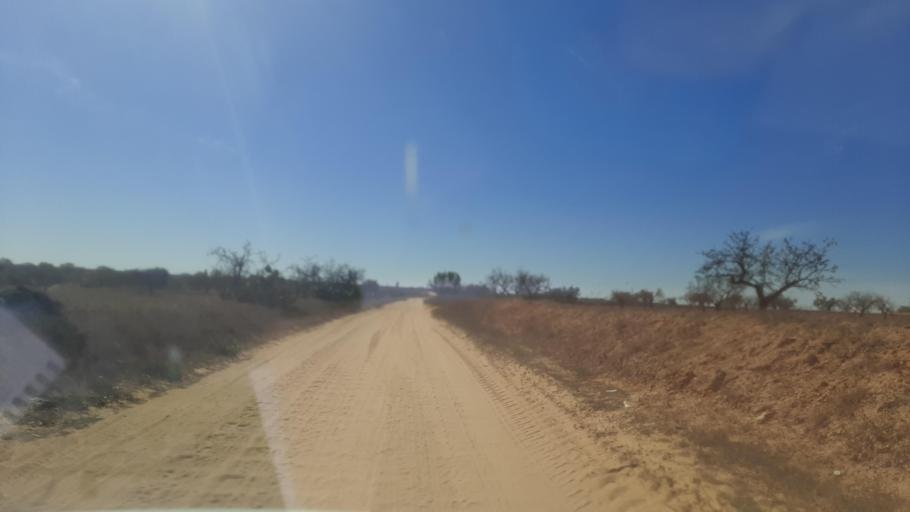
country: TN
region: Safaqis
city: Sfax
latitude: 34.8360
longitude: 10.5580
